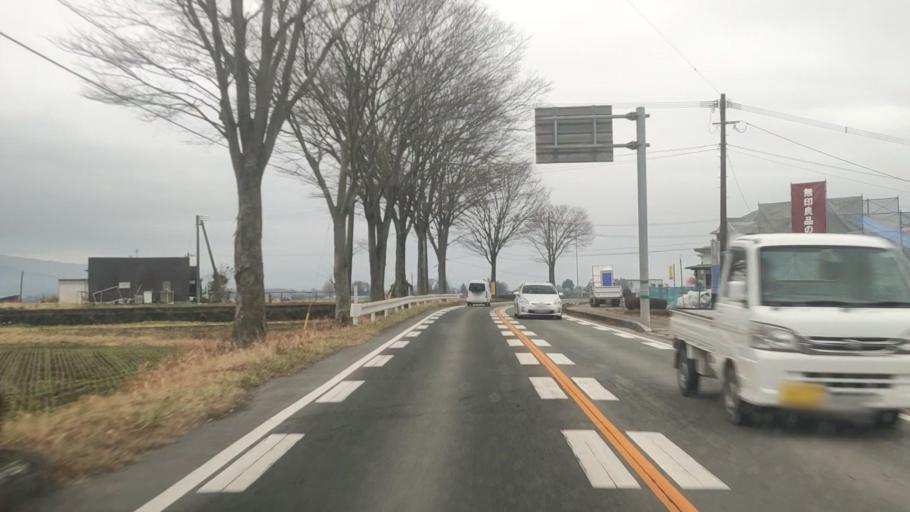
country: JP
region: Kumamoto
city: Aso
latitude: 32.9696
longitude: 131.0470
